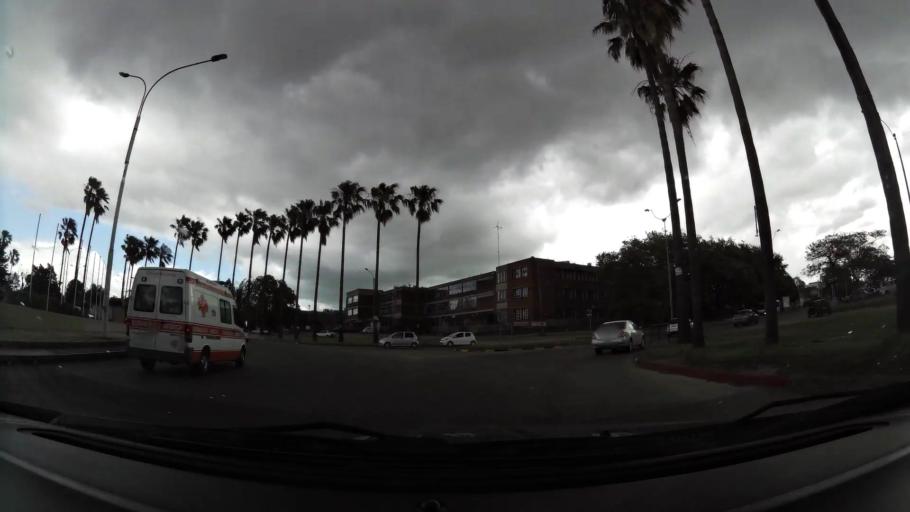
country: UY
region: Montevideo
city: Montevideo
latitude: -34.8628
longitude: -56.1685
